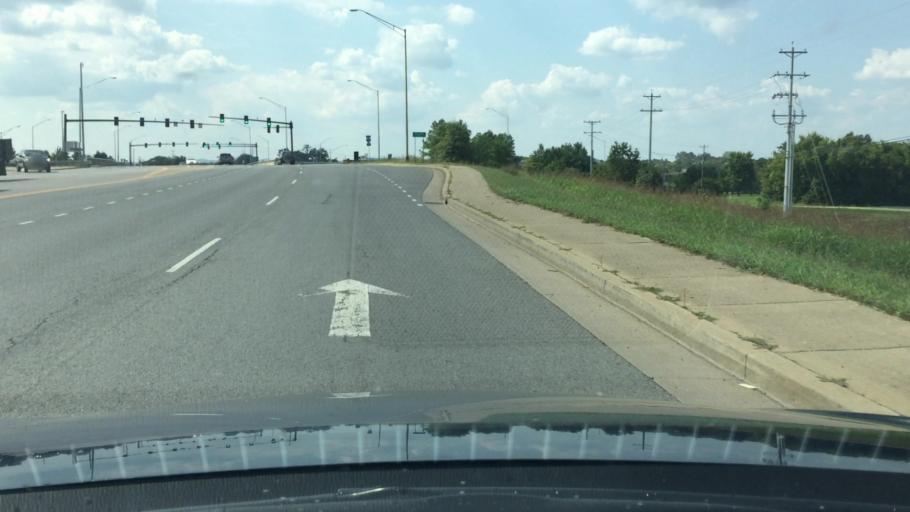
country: US
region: Tennessee
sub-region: Rutherford County
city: Murfreesboro
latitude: 35.8674
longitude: -86.4552
